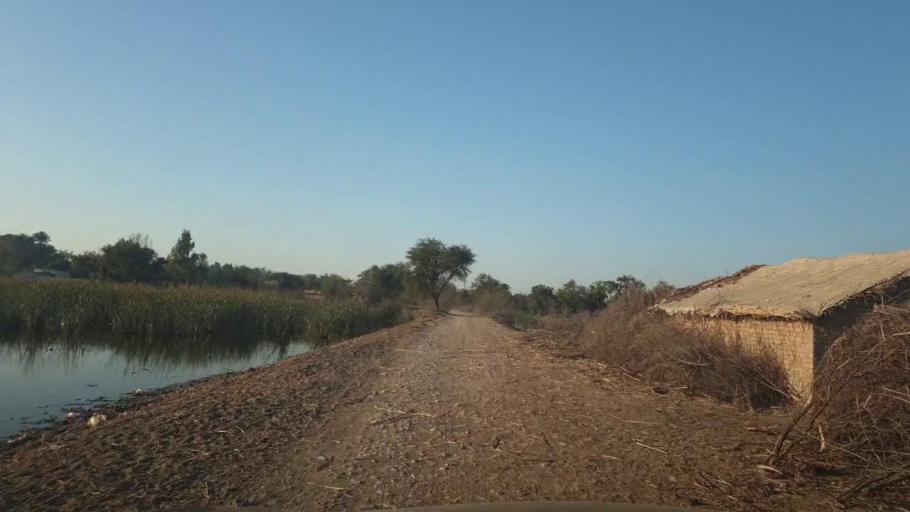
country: PK
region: Sindh
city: Mirpur Mathelo
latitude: 28.0033
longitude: 69.4665
